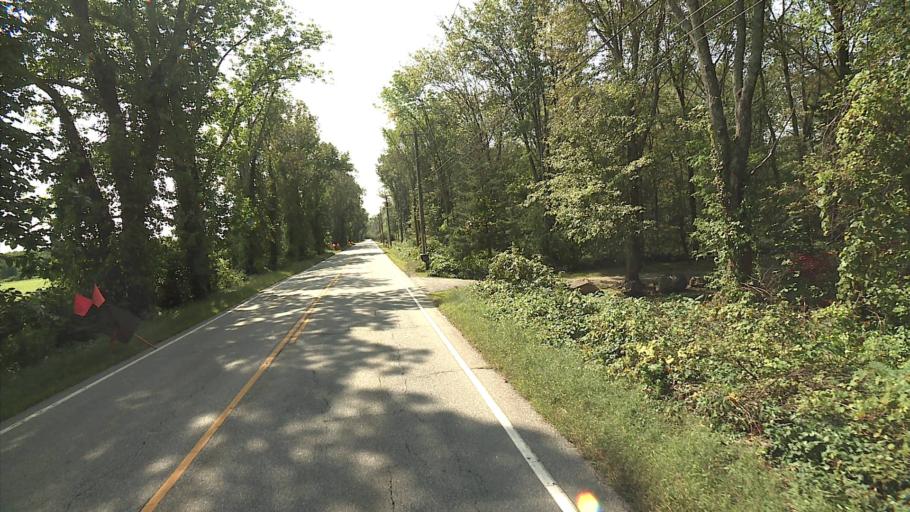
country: US
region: Connecticut
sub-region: Windham County
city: East Brooklyn
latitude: 41.8240
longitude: -71.9586
